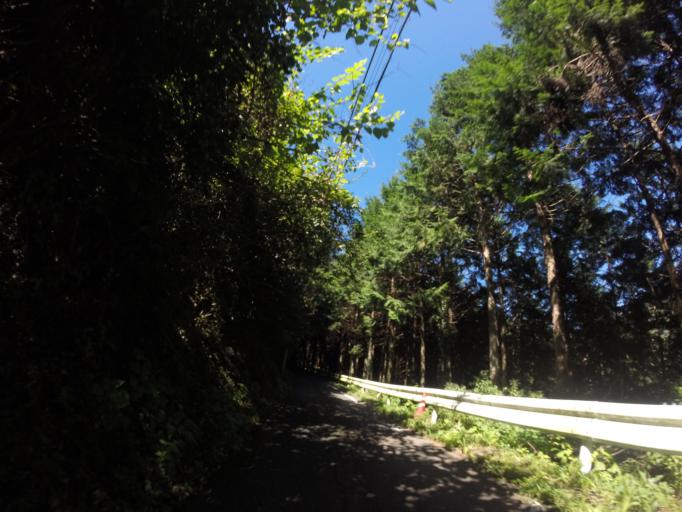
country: JP
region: Shizuoka
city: Fujieda
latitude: 34.9771
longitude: 138.1969
